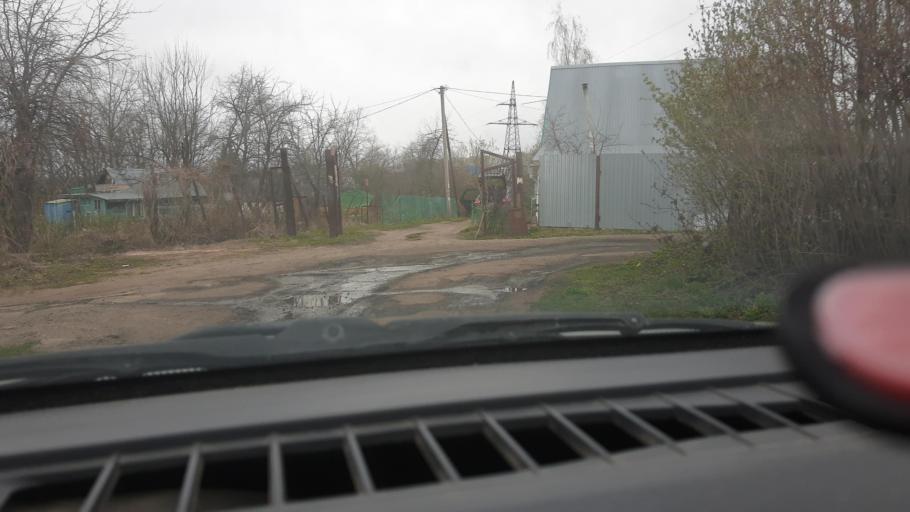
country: RU
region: Bashkortostan
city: Mikhaylovka
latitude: 54.9187
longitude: 55.8854
